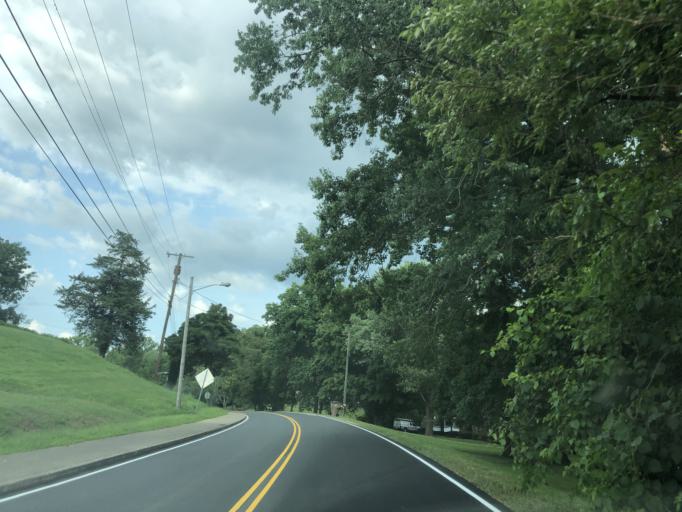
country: US
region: Tennessee
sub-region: Davidson County
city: Lakewood
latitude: 36.1591
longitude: -86.6806
